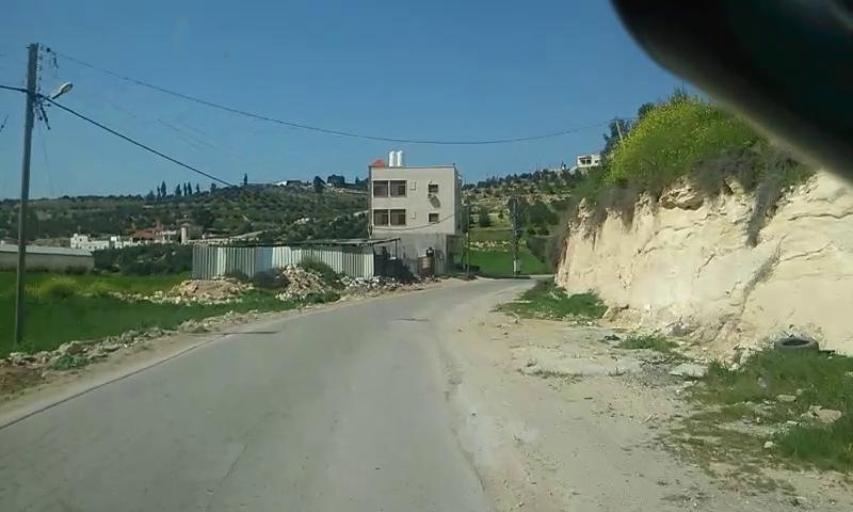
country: PS
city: Bayt Maqdum
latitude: 31.5460
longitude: 34.9636
